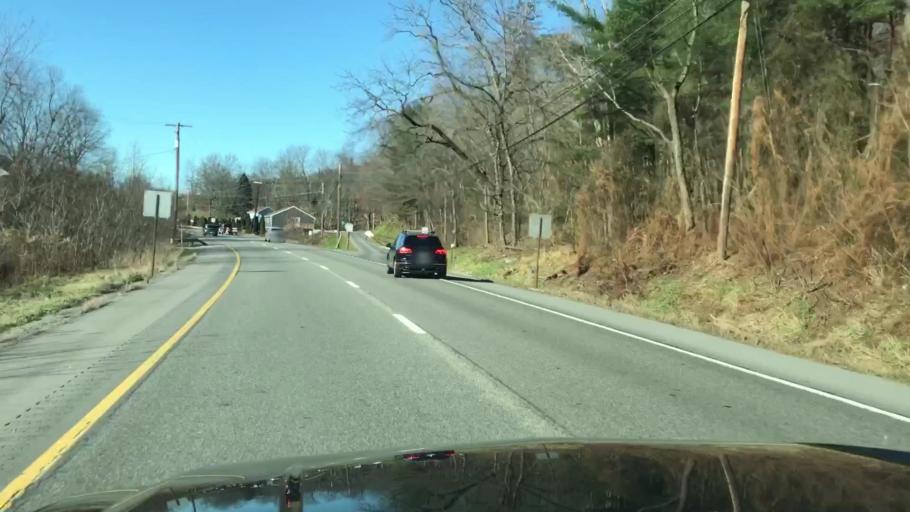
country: US
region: Pennsylvania
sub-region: Snyder County
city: Shamokin Dam
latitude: 40.8738
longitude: -76.8261
